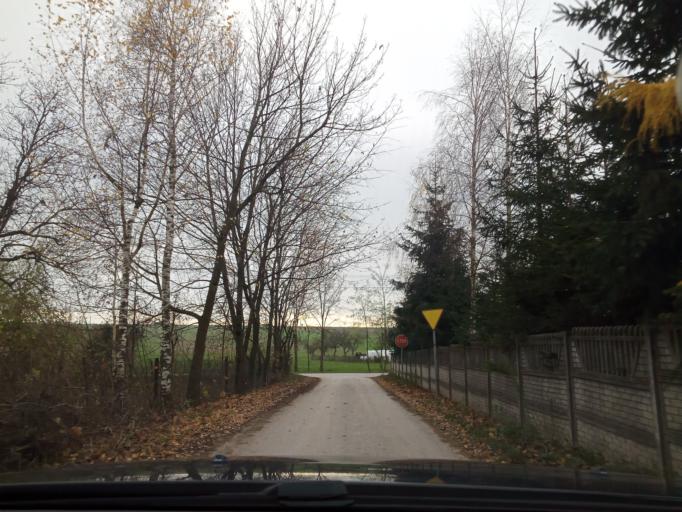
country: PL
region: Swietokrzyskie
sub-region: Powiat jedrzejowski
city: Imielno
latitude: 50.6106
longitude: 20.3902
